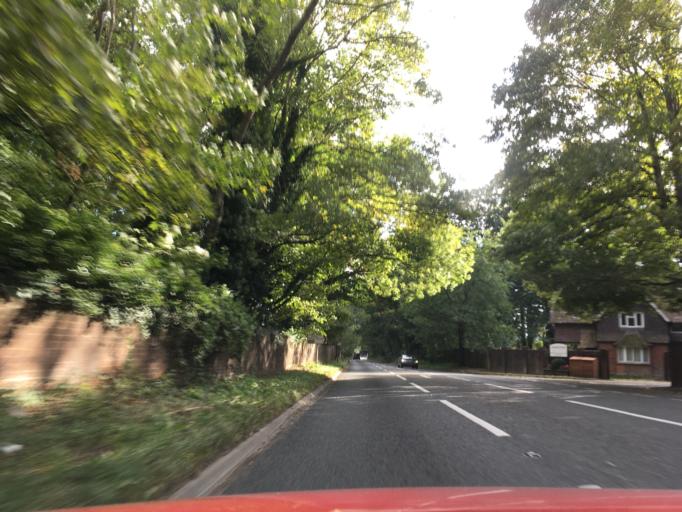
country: GB
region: England
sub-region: Hampshire
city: Basingstoke
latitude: 51.2461
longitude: -1.0793
